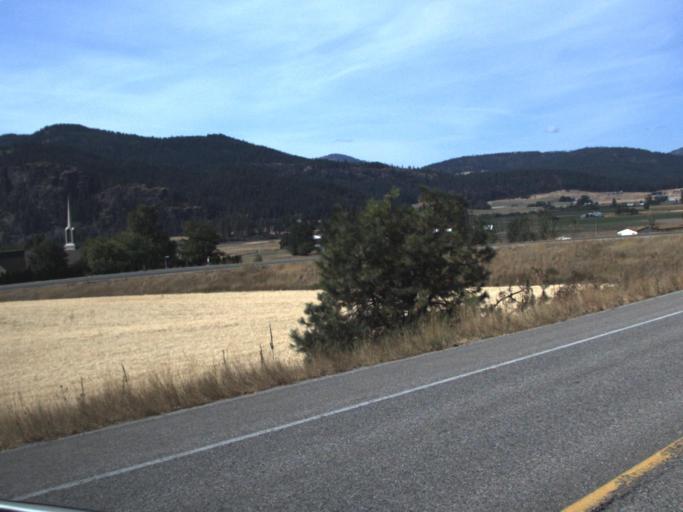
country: US
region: Washington
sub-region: Stevens County
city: Chewelah
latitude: 48.2967
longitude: -117.7510
